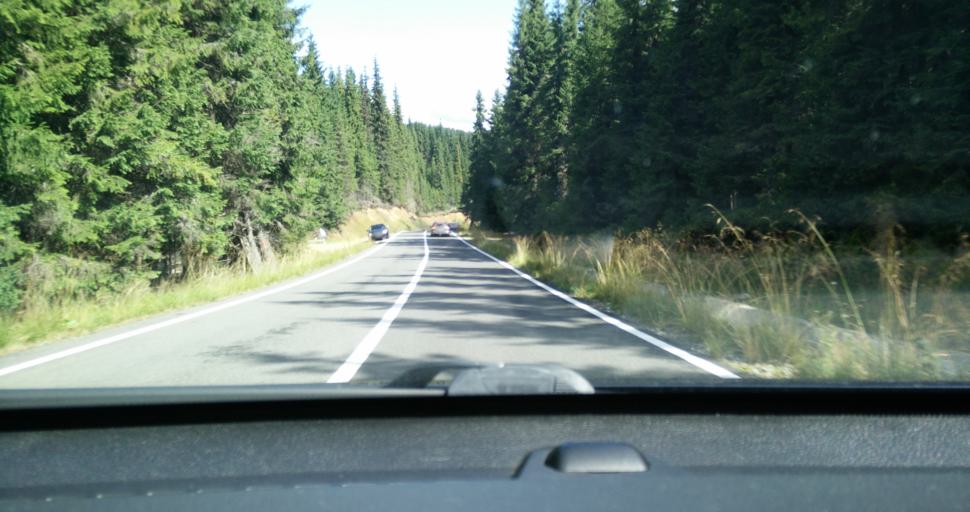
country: RO
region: Hunedoara
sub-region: Oras Petrila
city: Petrila
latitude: 45.4949
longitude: 23.6384
